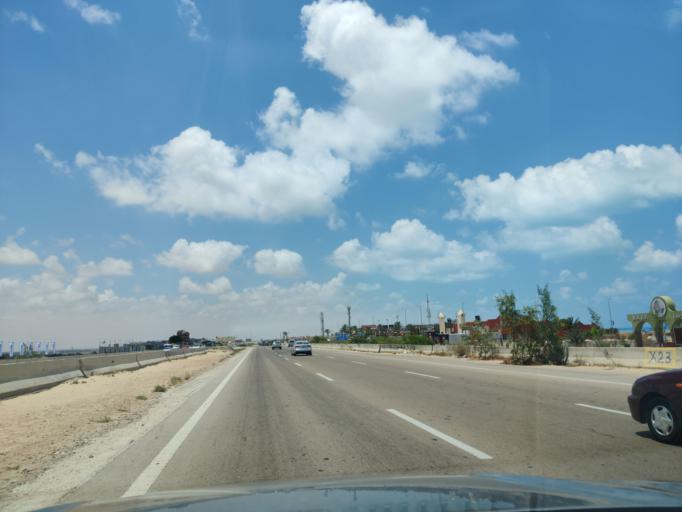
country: EG
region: Muhafazat Matruh
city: Al `Alamayn
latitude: 30.8222
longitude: 29.1765
